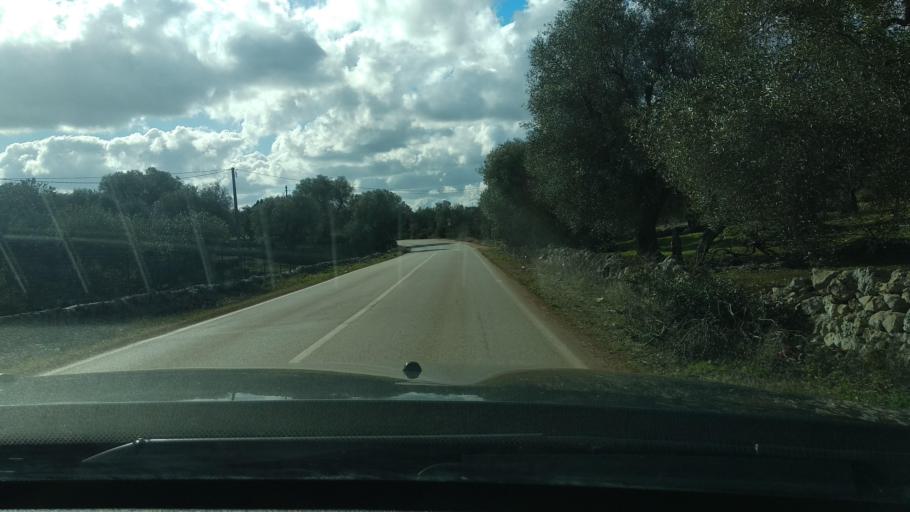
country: IT
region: Apulia
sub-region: Provincia di Brindisi
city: Casalini
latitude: 40.6934
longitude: 17.4795
